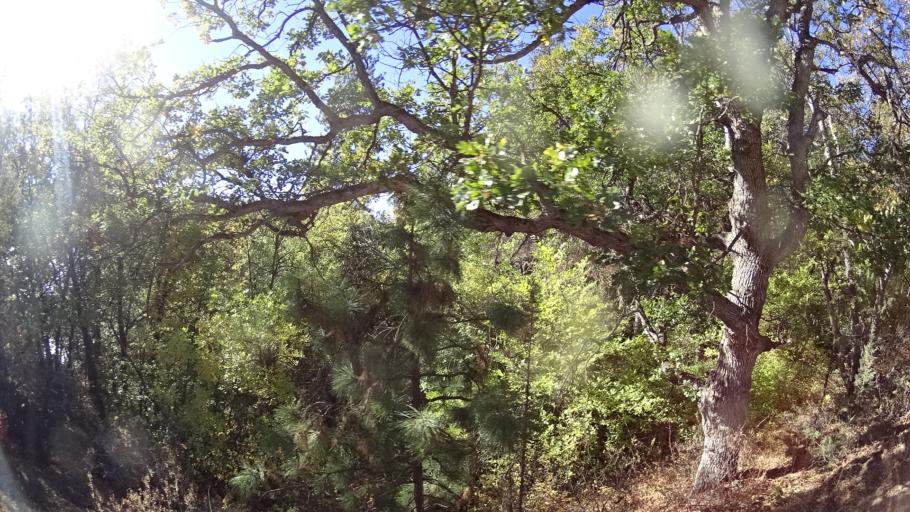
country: US
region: California
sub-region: Siskiyou County
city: Montague
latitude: 41.9857
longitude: -122.3313
